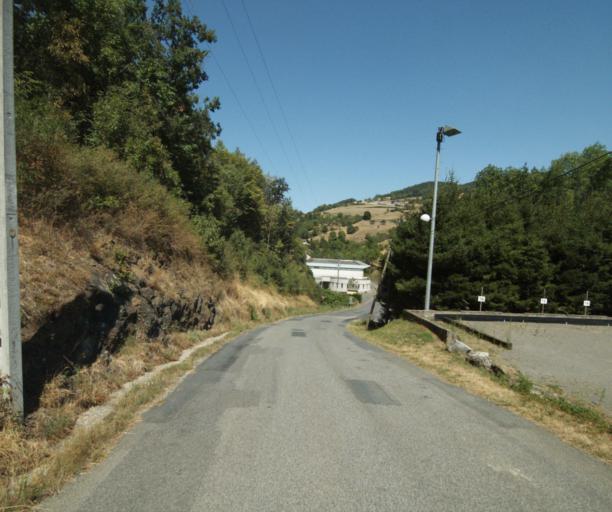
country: FR
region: Rhone-Alpes
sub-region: Departement du Rhone
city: Courzieu
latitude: 45.7378
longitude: 4.5661
